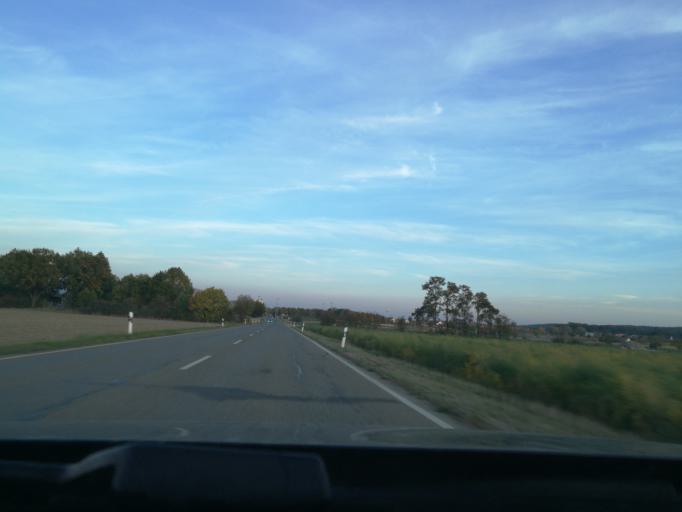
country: DE
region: Bavaria
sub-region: Regierungsbezirk Mittelfranken
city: Veitsbronn
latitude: 49.4977
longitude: 10.9016
